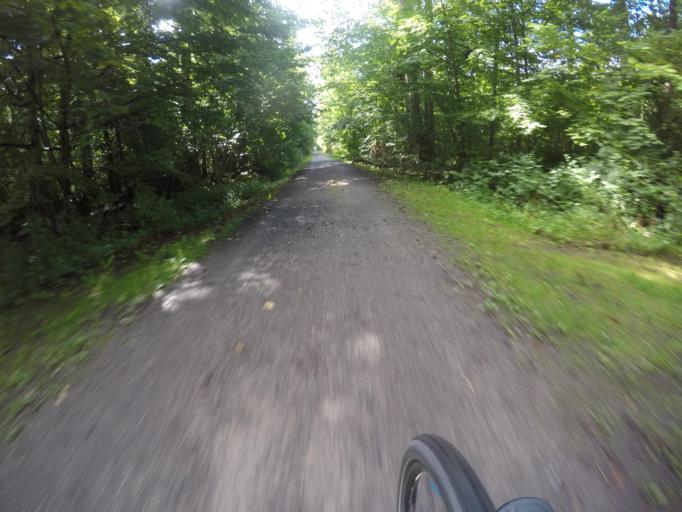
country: DE
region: Baden-Wuerttemberg
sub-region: Regierungsbezirk Stuttgart
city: Ehningen
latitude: 48.6764
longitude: 8.9503
